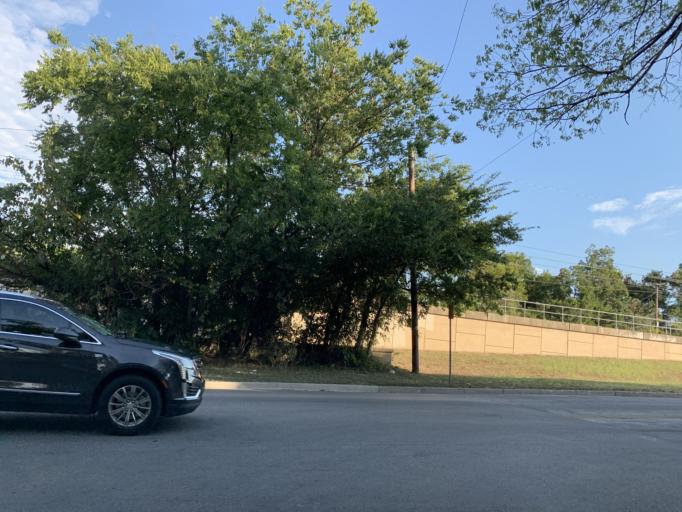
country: US
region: Texas
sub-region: Dallas County
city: Dallas
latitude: 32.7351
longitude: -96.8203
